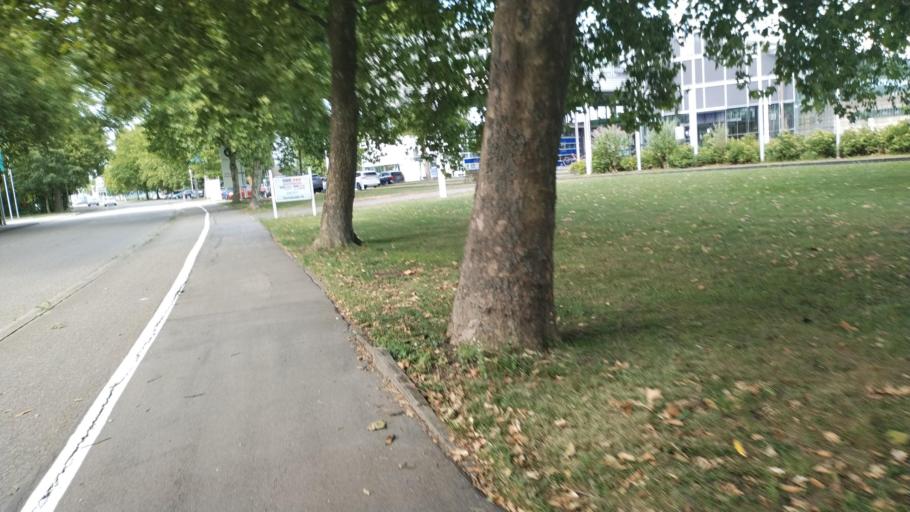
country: DE
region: Baden-Wuerttemberg
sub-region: Karlsruhe Region
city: Ettlingen
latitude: 48.9375
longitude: 8.3806
